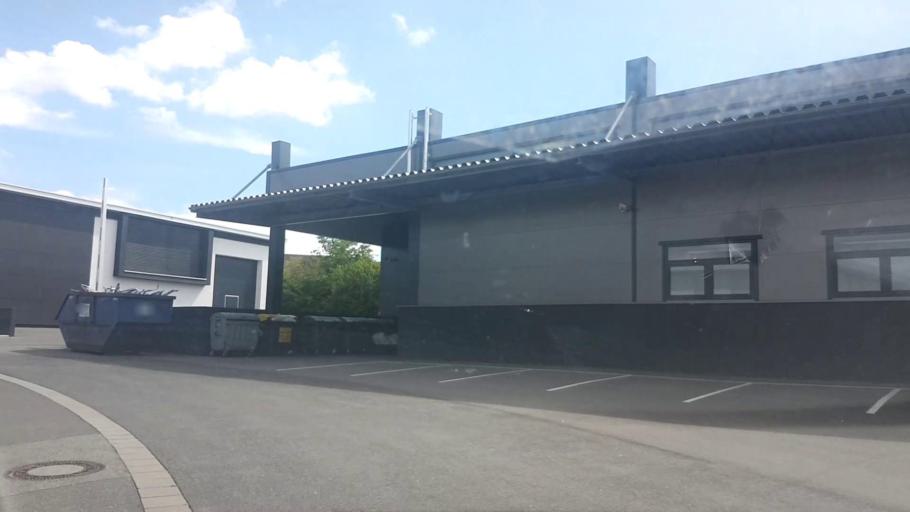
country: DE
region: Bavaria
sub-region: Upper Franconia
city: Untersiemau
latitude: 50.1974
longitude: 10.9636
